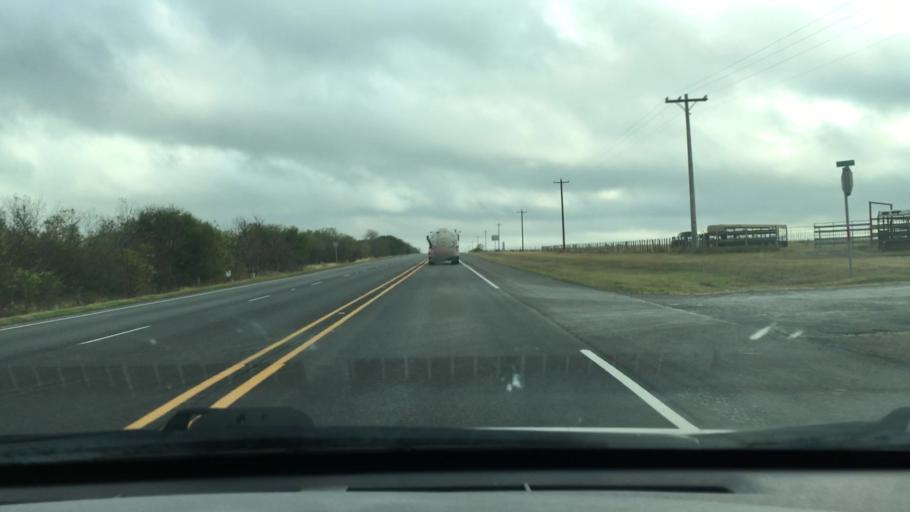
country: US
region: Texas
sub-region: Gonzales County
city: Nixon
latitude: 29.2587
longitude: -97.8027
